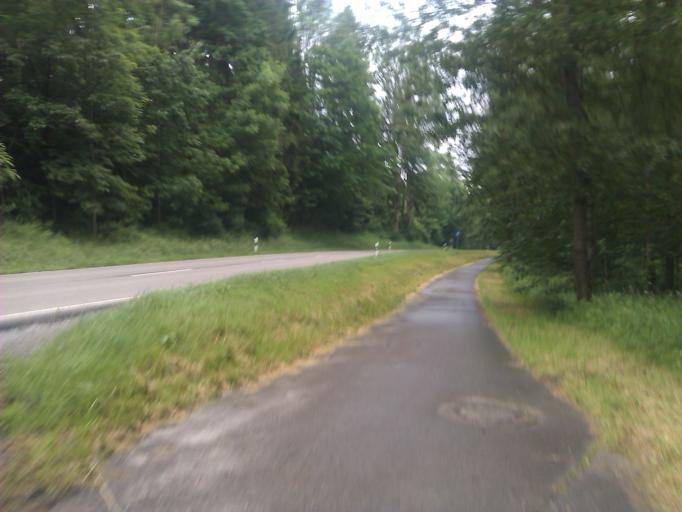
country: DE
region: Baden-Wuerttemberg
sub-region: Regierungsbezirk Stuttgart
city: Fichtenberg
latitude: 48.9952
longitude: 9.6894
